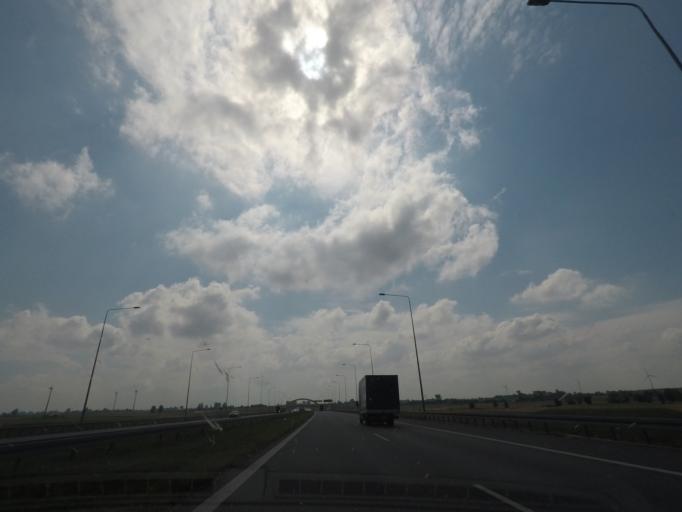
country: PL
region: Lodz Voivodeship
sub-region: Powiat kutnowski
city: Krzyzanow
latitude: 52.2292
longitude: 19.4597
